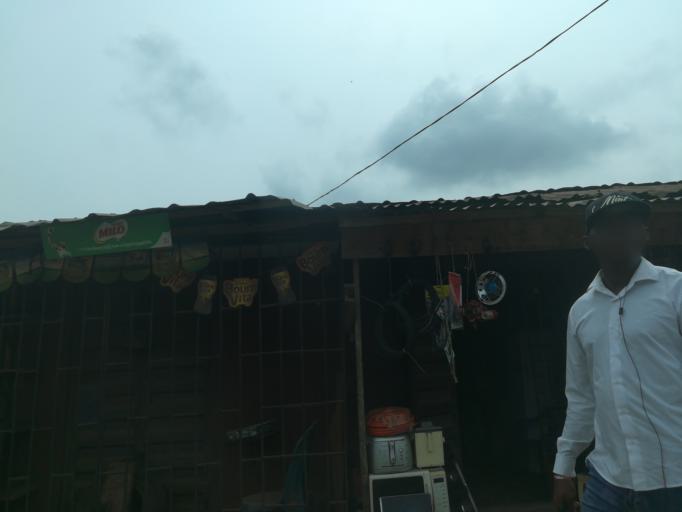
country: NG
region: Lagos
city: Ojota
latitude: 6.6098
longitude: 3.4144
